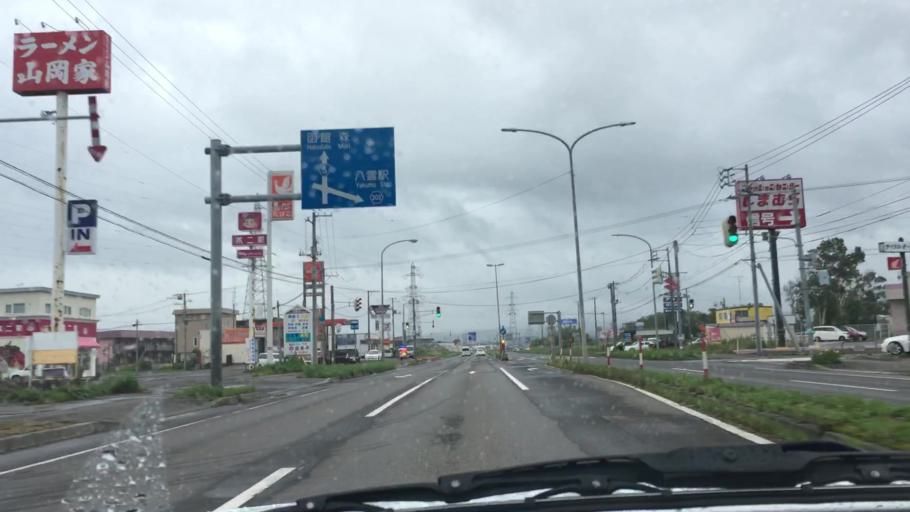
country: JP
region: Hokkaido
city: Nanae
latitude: 42.2570
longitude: 140.2798
